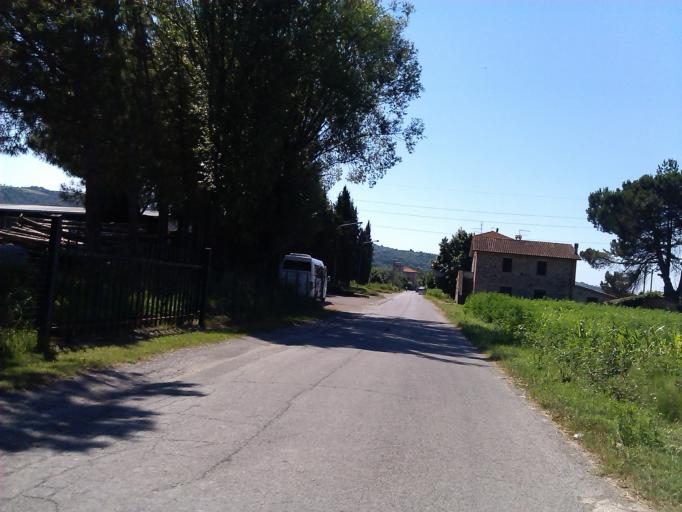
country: IT
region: Umbria
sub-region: Provincia di Terni
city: Fabro Scalo
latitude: 42.8746
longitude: 12.0392
